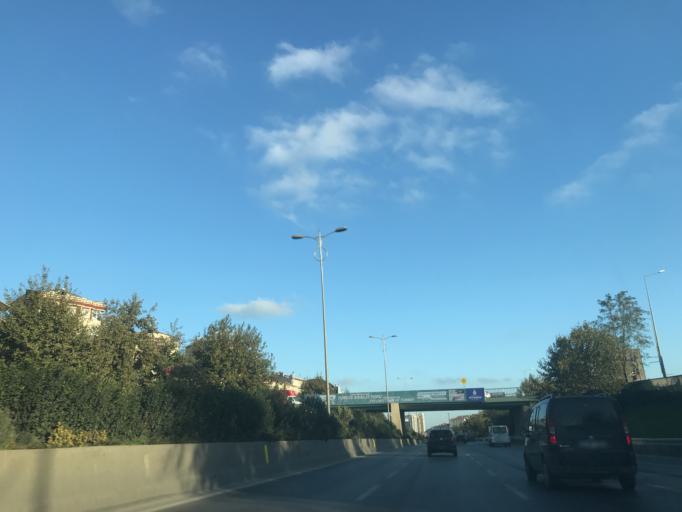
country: TR
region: Istanbul
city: Esenler
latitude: 41.0503
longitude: 28.8728
